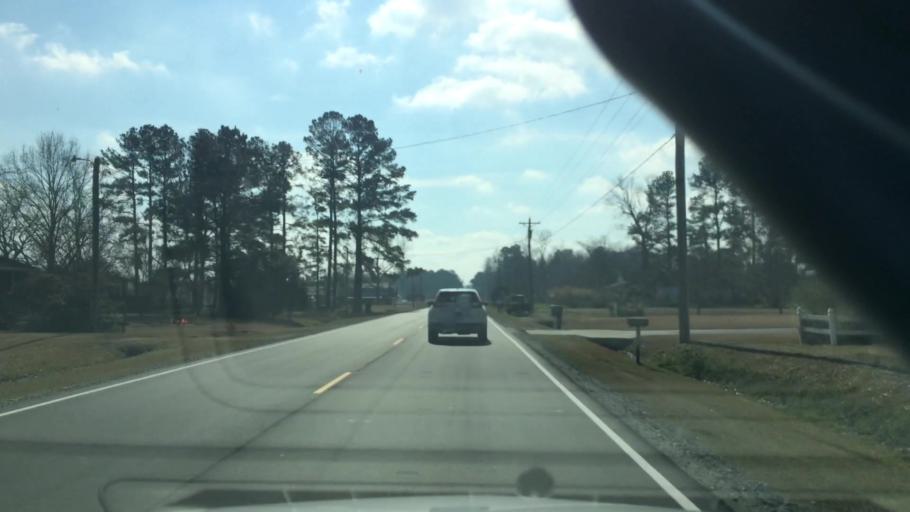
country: US
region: North Carolina
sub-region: Duplin County
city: Beulaville
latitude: 34.9716
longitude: -77.7621
